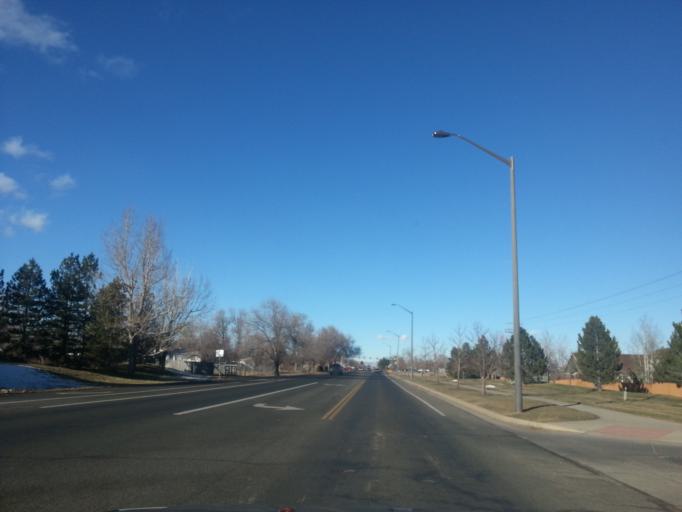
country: US
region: Colorado
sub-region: Larimer County
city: Fort Collins
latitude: 40.5283
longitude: -105.1151
